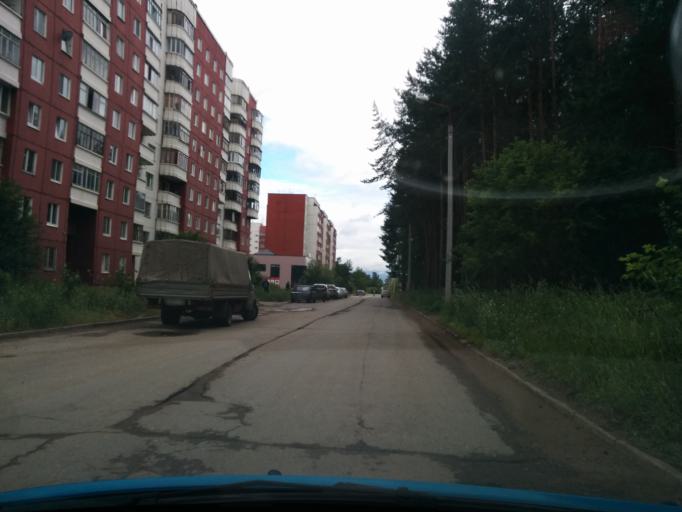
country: RU
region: Perm
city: Kondratovo
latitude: 58.0235
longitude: 56.0023
